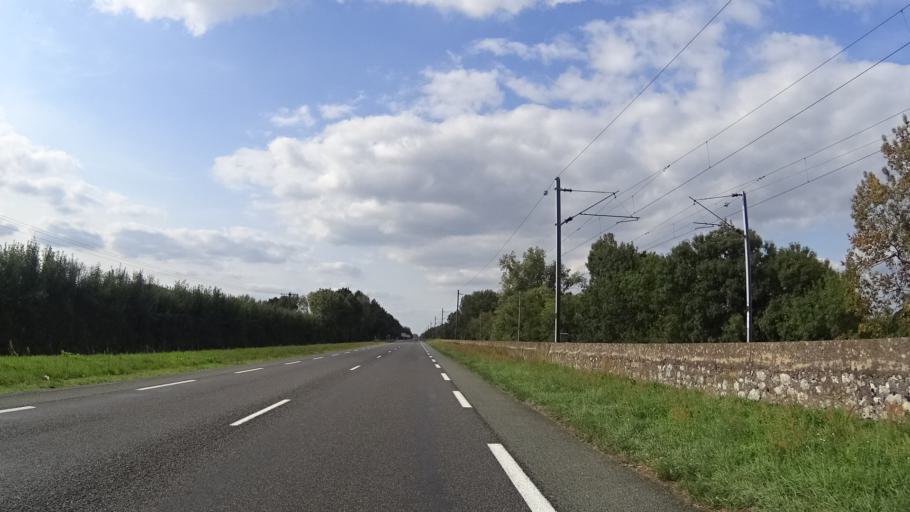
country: FR
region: Pays de la Loire
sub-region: Departement de Maine-et-Loire
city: Saumur
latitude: 47.2899
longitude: -0.1054
